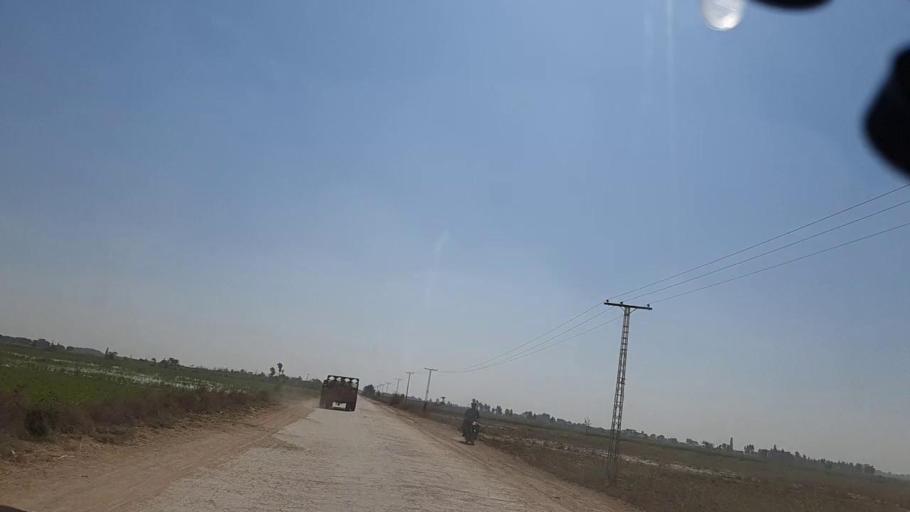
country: PK
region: Sindh
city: Mirpur Khas
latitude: 25.5019
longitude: 69.0339
